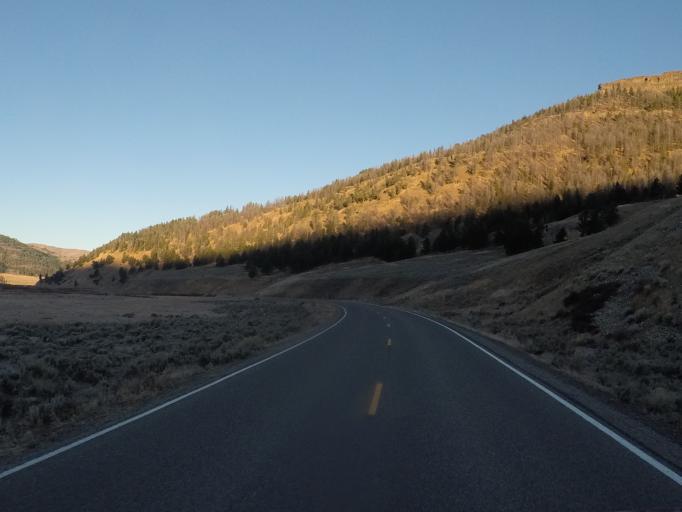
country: US
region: Montana
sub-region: Park County
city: Livingston
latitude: 44.9093
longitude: -110.1152
